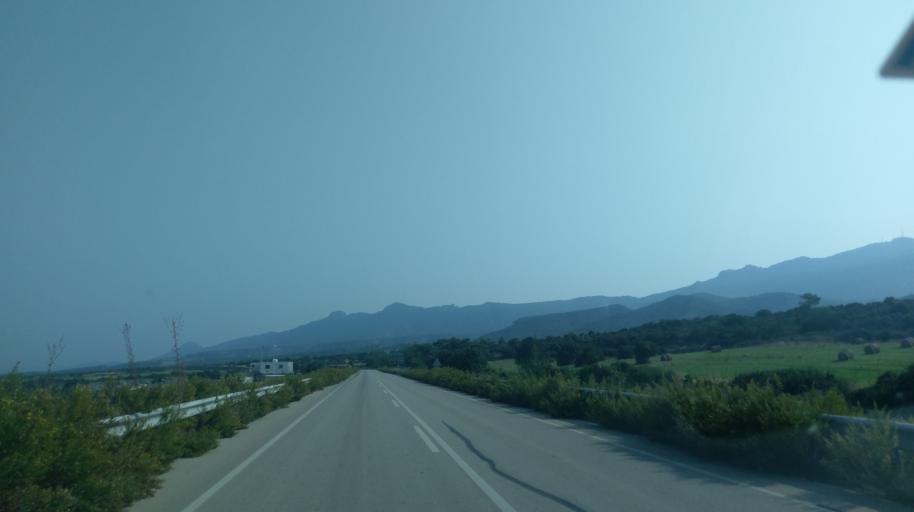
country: CY
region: Ammochostos
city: Trikomo
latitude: 35.4116
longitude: 33.8475
